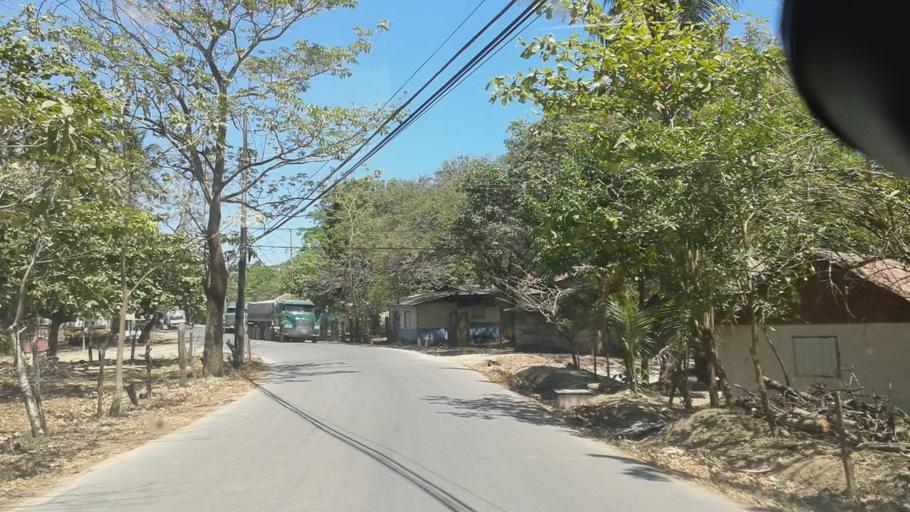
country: CR
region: Guanacaste
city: Samara
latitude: 9.9103
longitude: -85.6456
